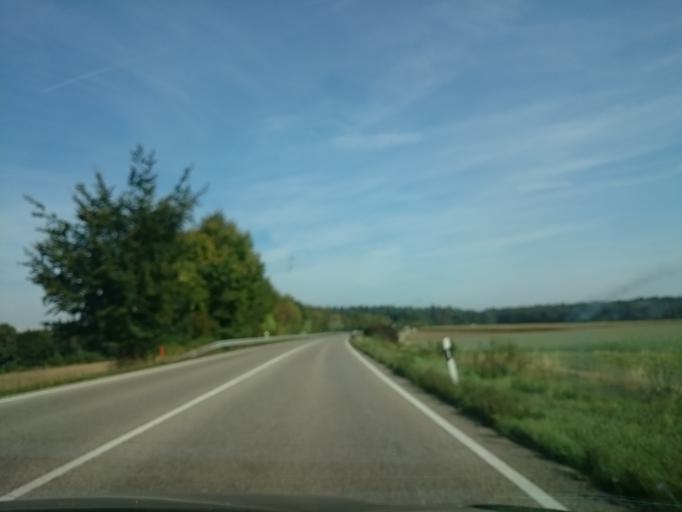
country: DE
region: Bavaria
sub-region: Swabia
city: Kuhbach
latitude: 48.4984
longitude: 11.2065
